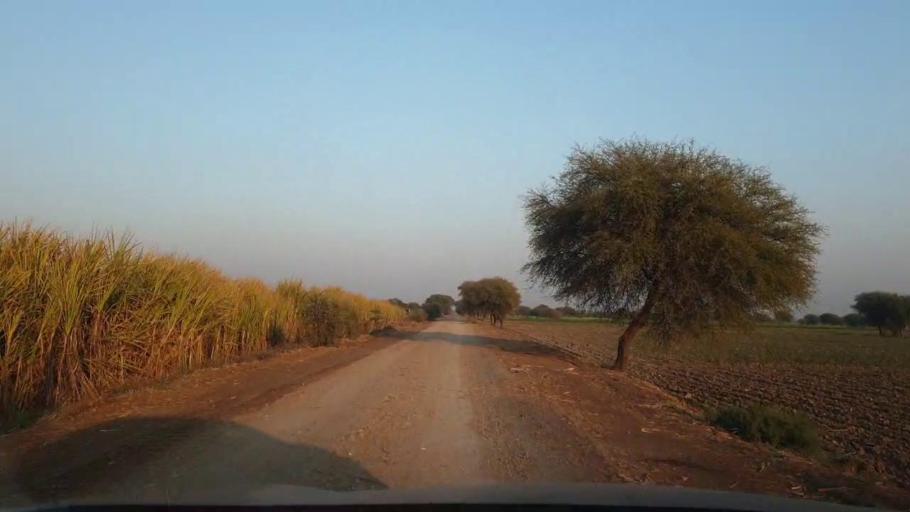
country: PK
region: Sindh
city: Mirpur Khas
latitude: 25.5758
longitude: 68.8528
